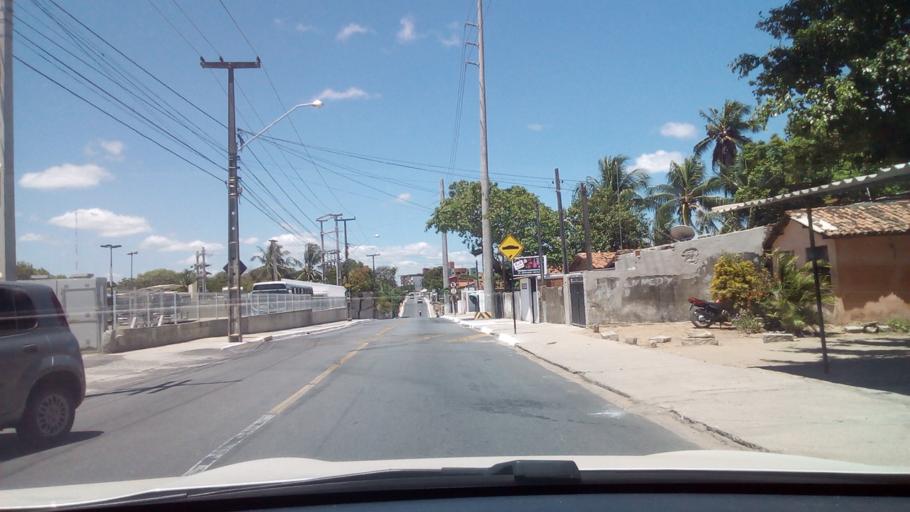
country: BR
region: Paraiba
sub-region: Joao Pessoa
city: Joao Pessoa
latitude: -7.1607
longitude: -34.8312
